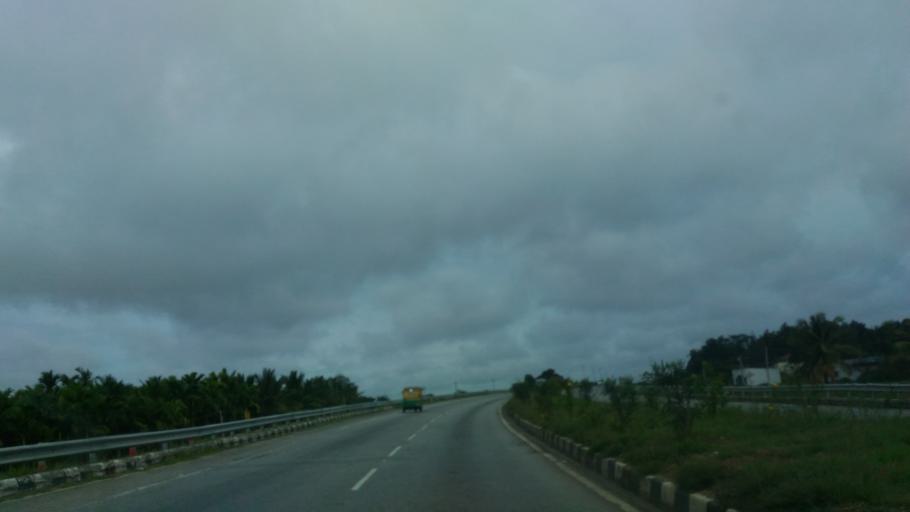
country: IN
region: Karnataka
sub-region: Tumkur
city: Kunigal
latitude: 13.0014
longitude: 76.9631
